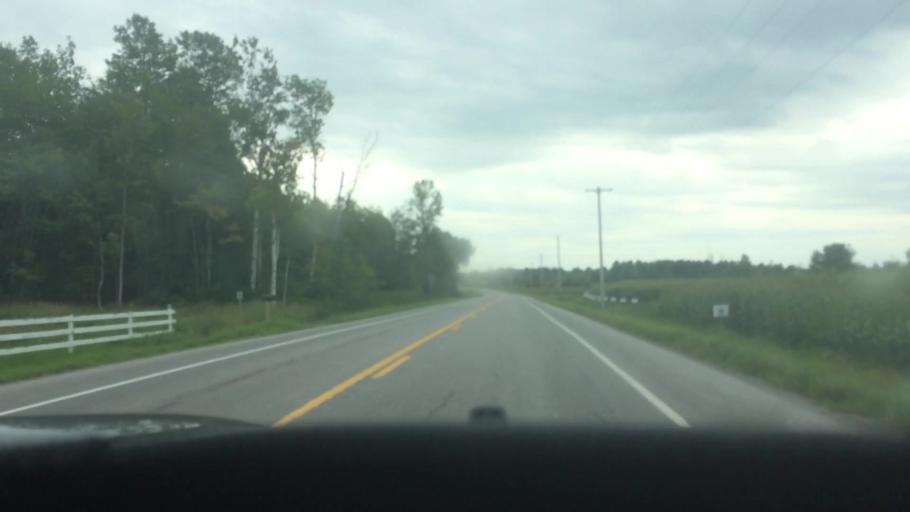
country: US
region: New York
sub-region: St. Lawrence County
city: Ogdensburg
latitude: 44.5823
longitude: -75.3704
